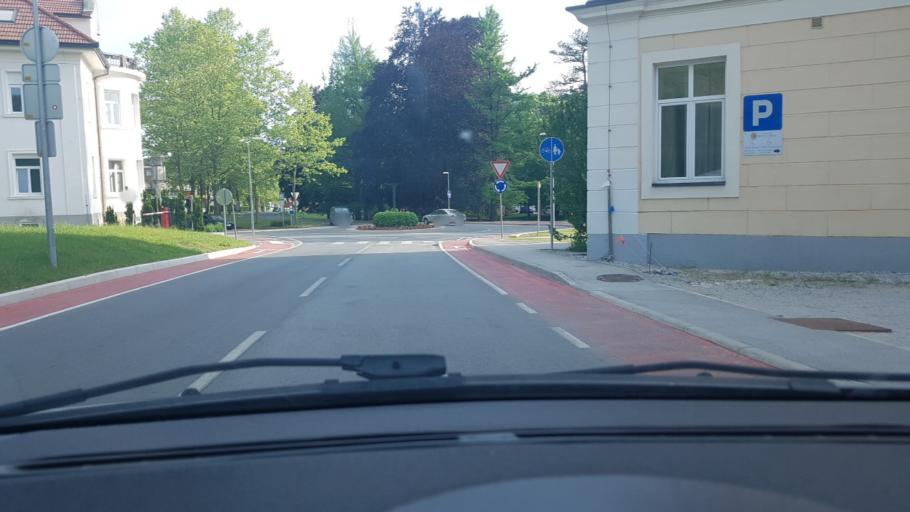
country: SI
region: Rogaska Slatina
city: Rogaska Slatina
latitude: 46.2362
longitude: 15.6390
